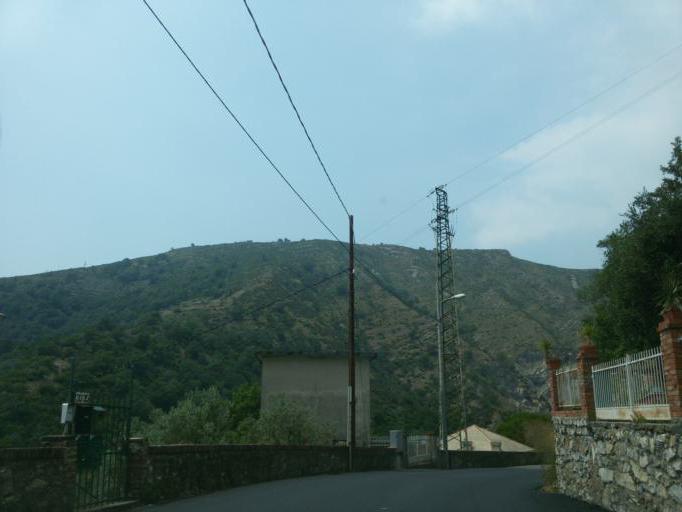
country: IT
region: Liguria
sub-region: Provincia di Genova
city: Piccarello
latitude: 44.4213
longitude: 9.0051
